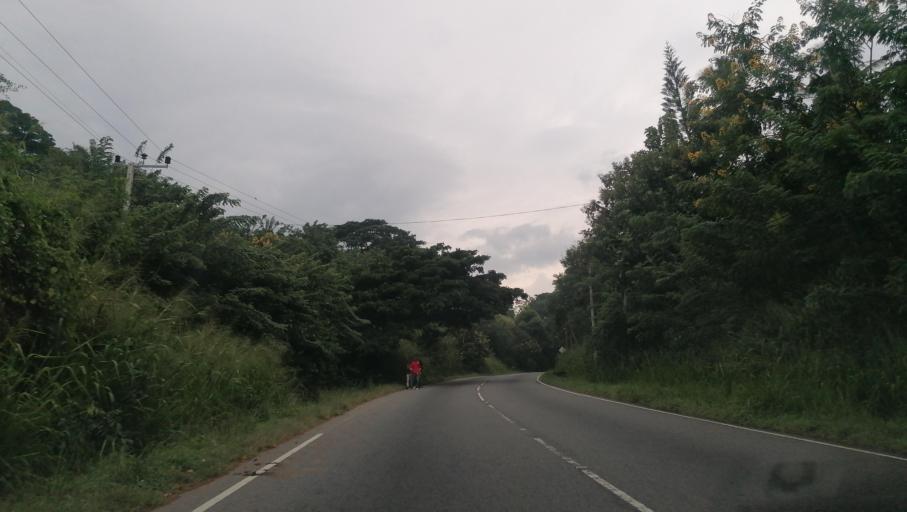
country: LK
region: Central
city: Kandy
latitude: 7.2522
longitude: 80.7311
